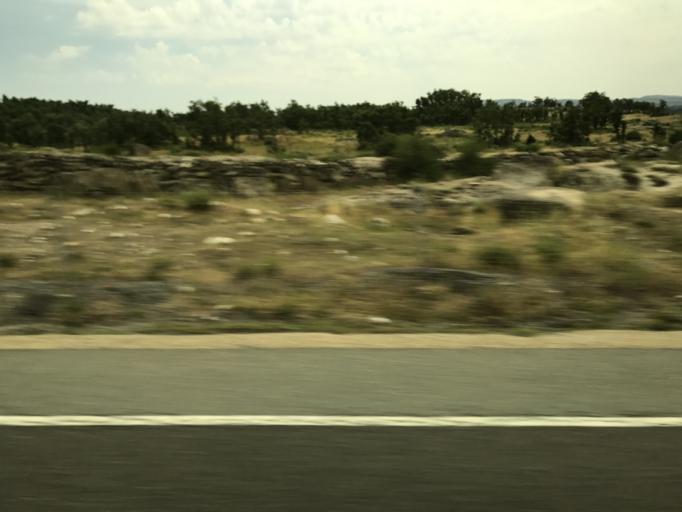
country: ES
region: Madrid
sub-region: Provincia de Madrid
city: La Cabrera
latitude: 40.9102
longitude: -3.6090
